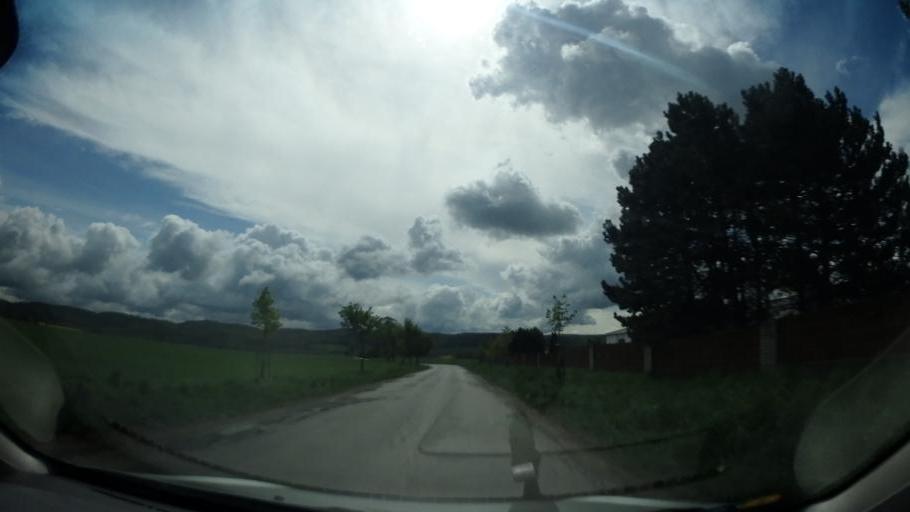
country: CZ
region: South Moravian
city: Ricany
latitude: 49.2307
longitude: 16.4108
